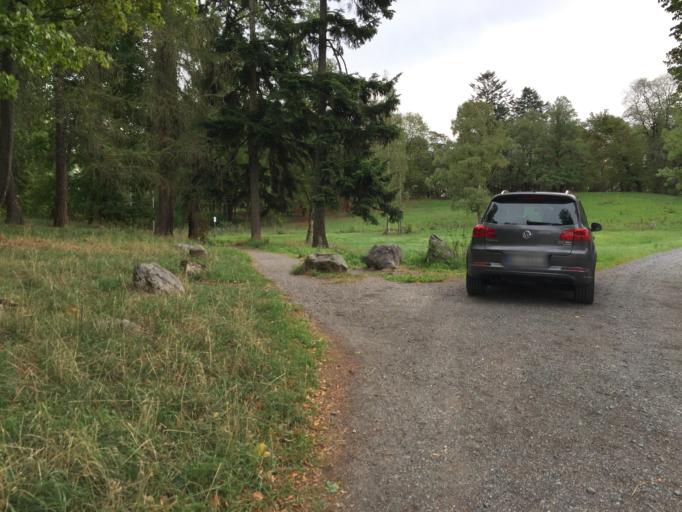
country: NO
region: Oslo
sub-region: Oslo
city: Sjolyststranda
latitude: 59.9139
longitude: 10.6881
